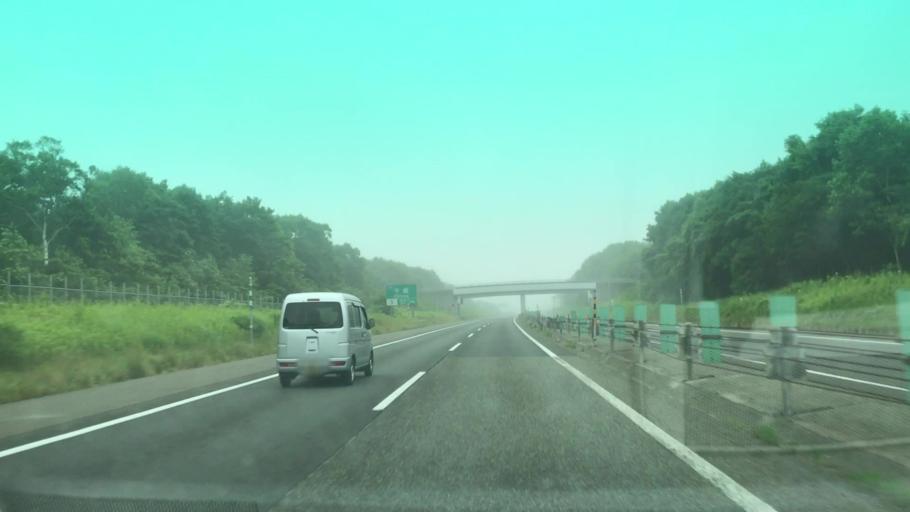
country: JP
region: Hokkaido
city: Chitose
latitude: 42.8248
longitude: 141.6155
